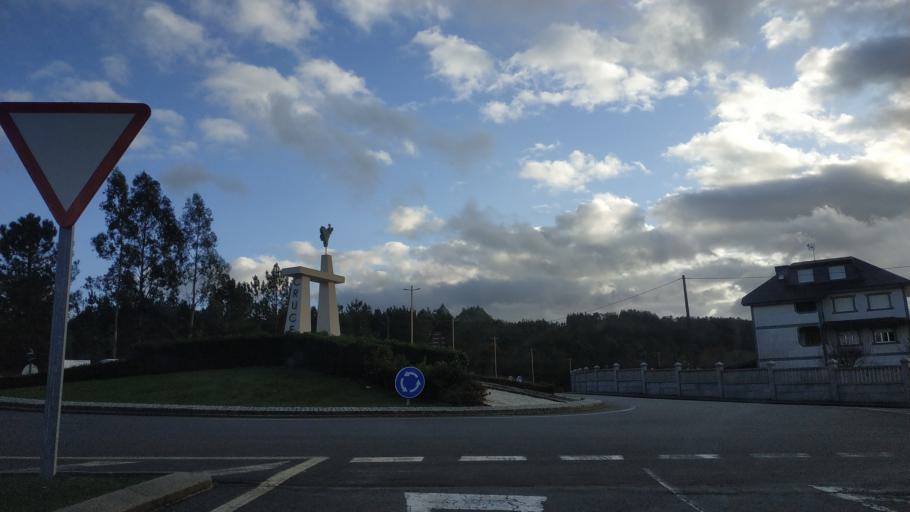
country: ES
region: Galicia
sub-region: Provincia de Pontevedra
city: Silleda
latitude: 42.7929
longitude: -8.1612
